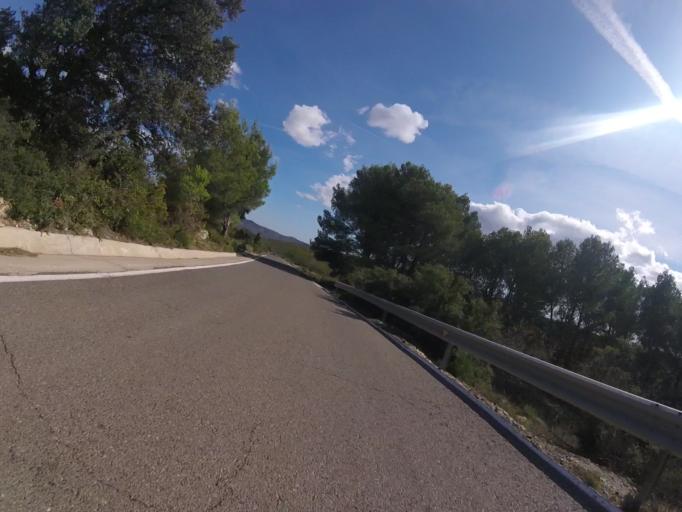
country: ES
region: Valencia
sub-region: Provincia de Castello
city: Albocasser
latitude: 40.3955
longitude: 0.0908
